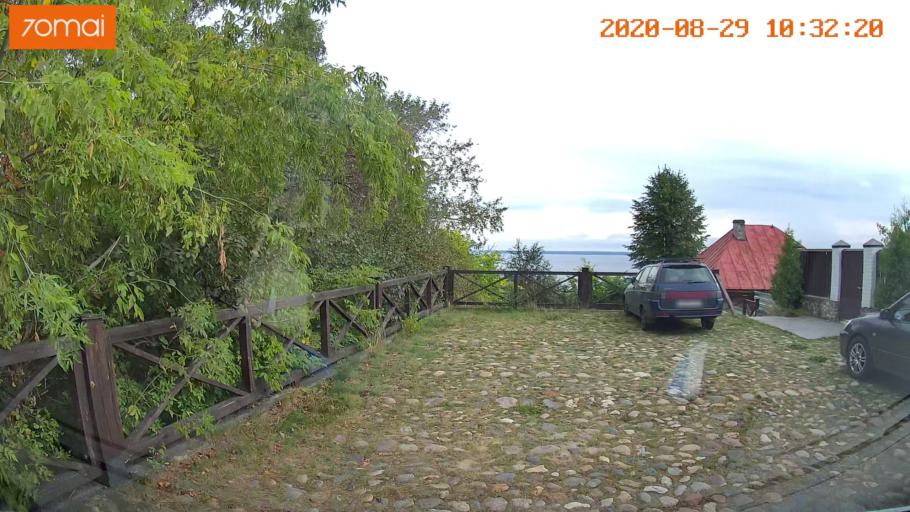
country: RU
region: Ivanovo
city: Yur'yevets
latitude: 57.3157
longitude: 43.1068
